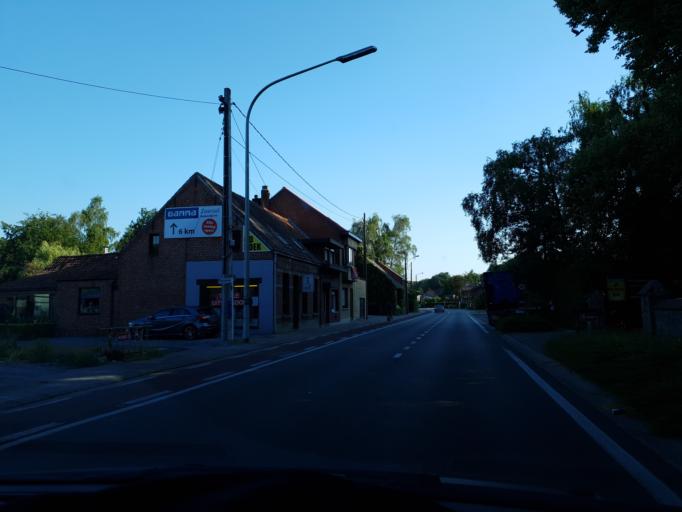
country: BE
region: Flanders
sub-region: Provincie Antwerpen
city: Oostmalle
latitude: 51.2982
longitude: 4.7324
